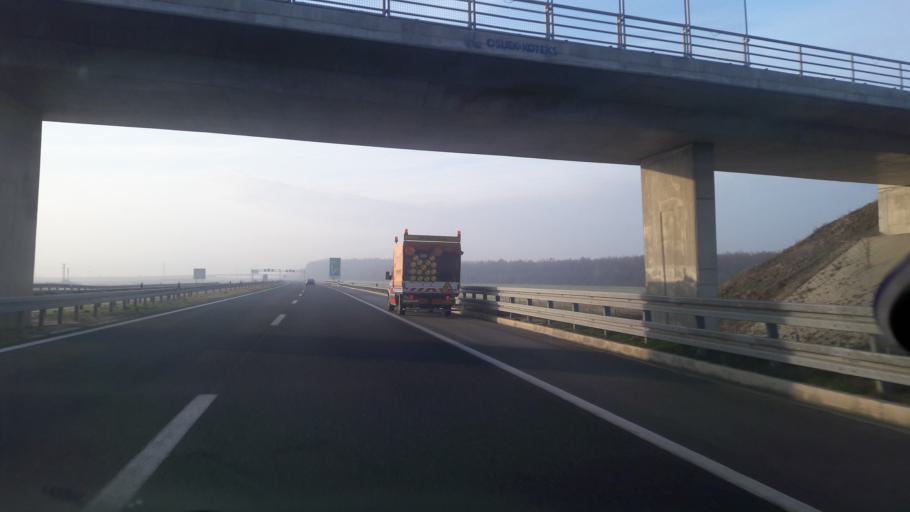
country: HR
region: Osjecko-Baranjska
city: Cepin
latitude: 45.5162
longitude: 18.5082
